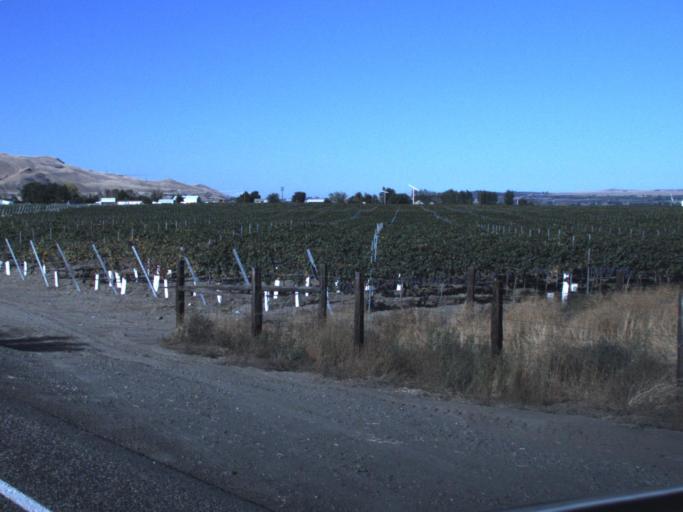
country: US
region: Washington
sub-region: Benton County
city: Benton City
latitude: 46.2684
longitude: -119.4415
